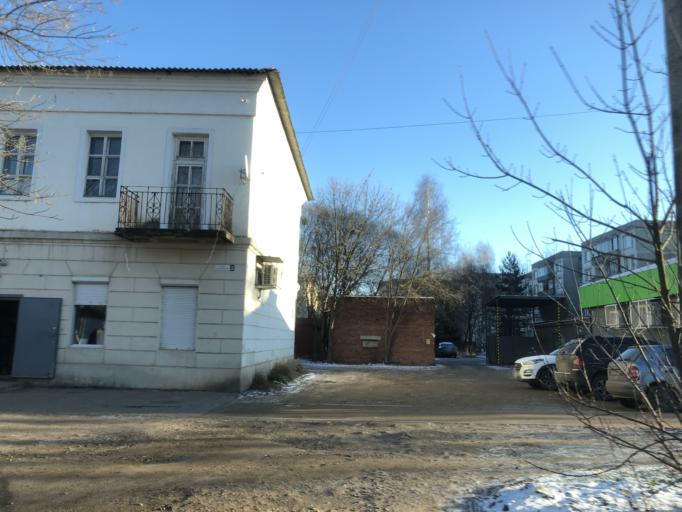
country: RU
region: Tverskaya
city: Rzhev
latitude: 56.2597
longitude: 34.3504
